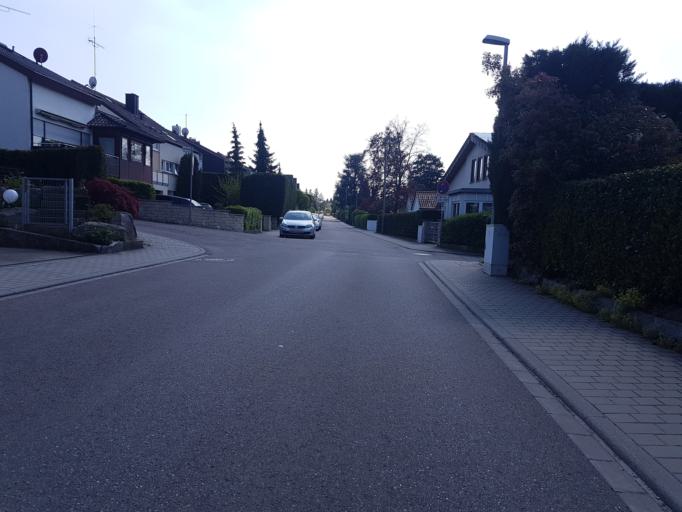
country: DE
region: Baden-Wuerttemberg
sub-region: Regierungsbezirk Stuttgart
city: Bietigheim-Bissingen
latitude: 48.9637
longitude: 9.1383
